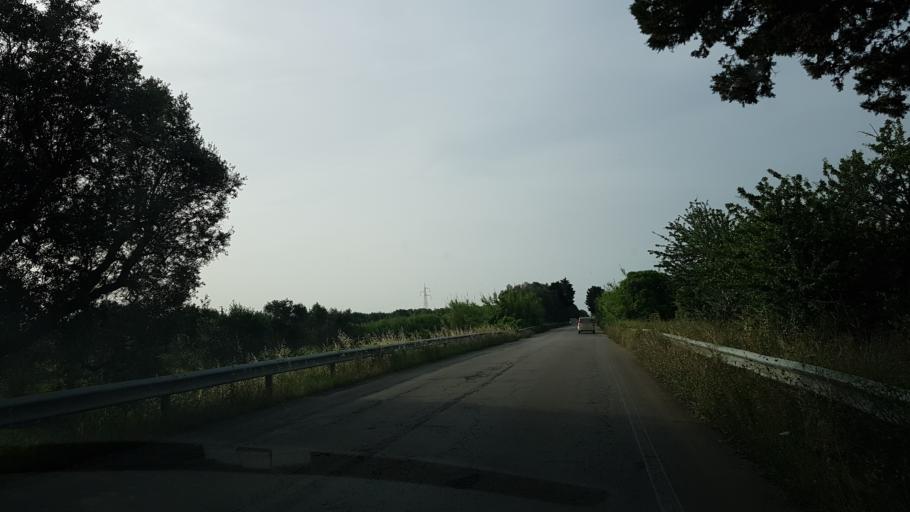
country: IT
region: Apulia
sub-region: Provincia di Brindisi
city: Tuturano
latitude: 40.5341
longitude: 17.9815
